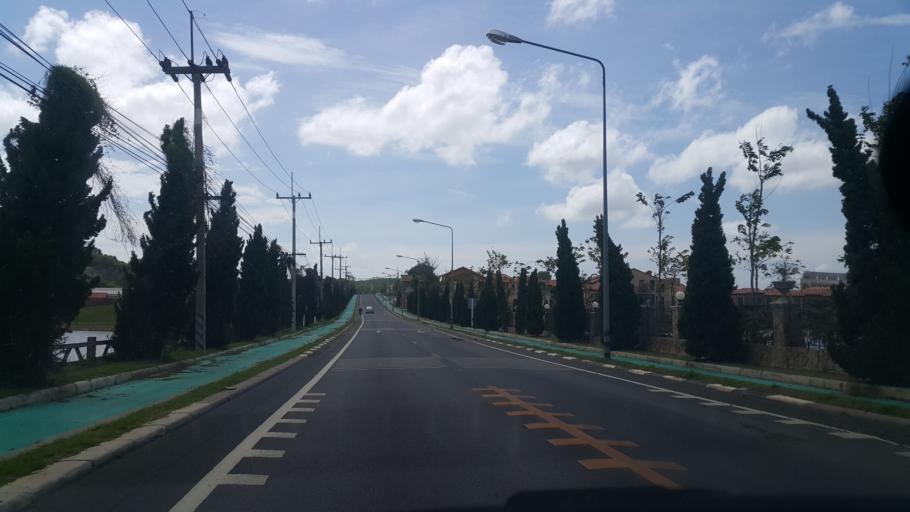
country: TH
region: Rayong
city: Ban Chang
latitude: 12.7620
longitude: 100.9631
